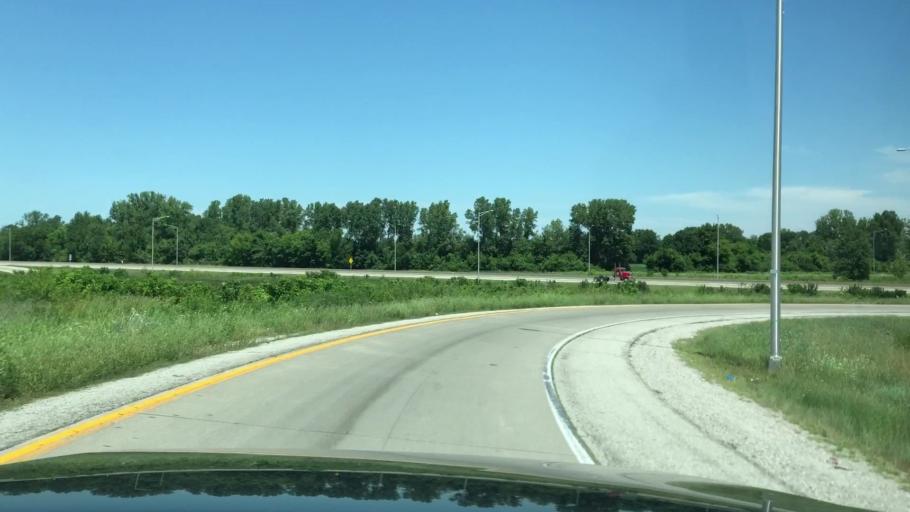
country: US
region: Illinois
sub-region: Saint Clair County
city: Alorton
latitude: 38.5828
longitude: -90.1107
